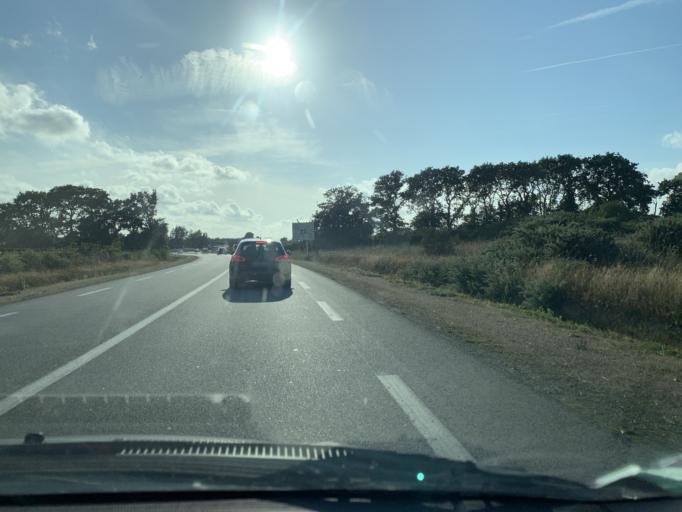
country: FR
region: Brittany
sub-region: Departement du Morbihan
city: Sarzeau
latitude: 47.5517
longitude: -2.7133
